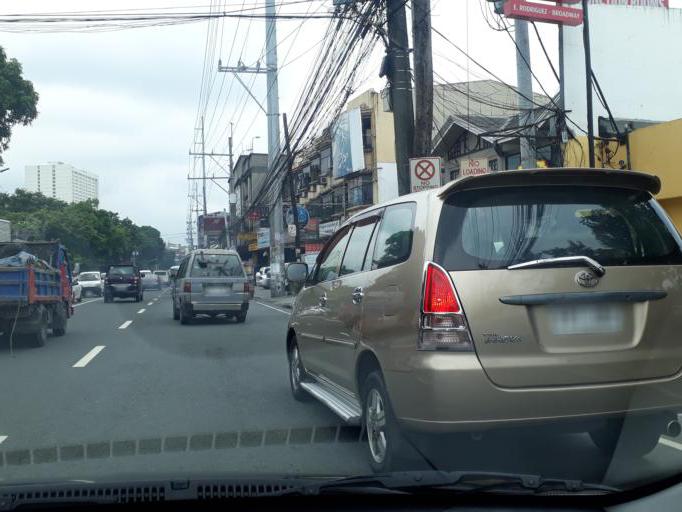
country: PH
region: Calabarzon
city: Del Monte
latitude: 14.6224
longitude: 121.0266
